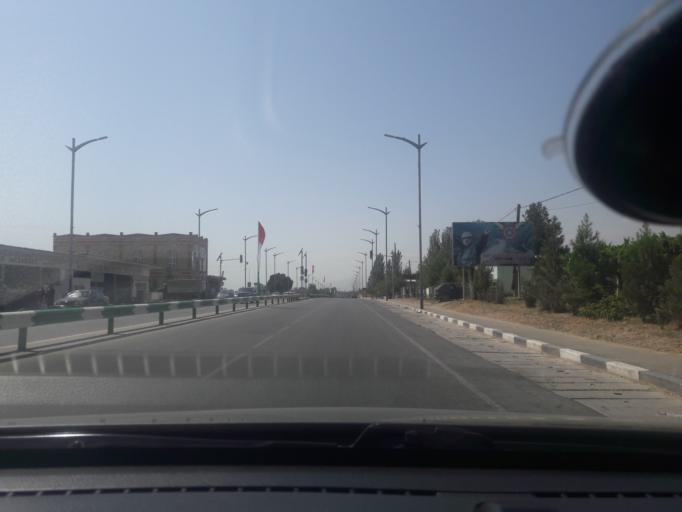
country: TJ
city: Shahrinav
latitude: 38.5621
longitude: 68.4220
